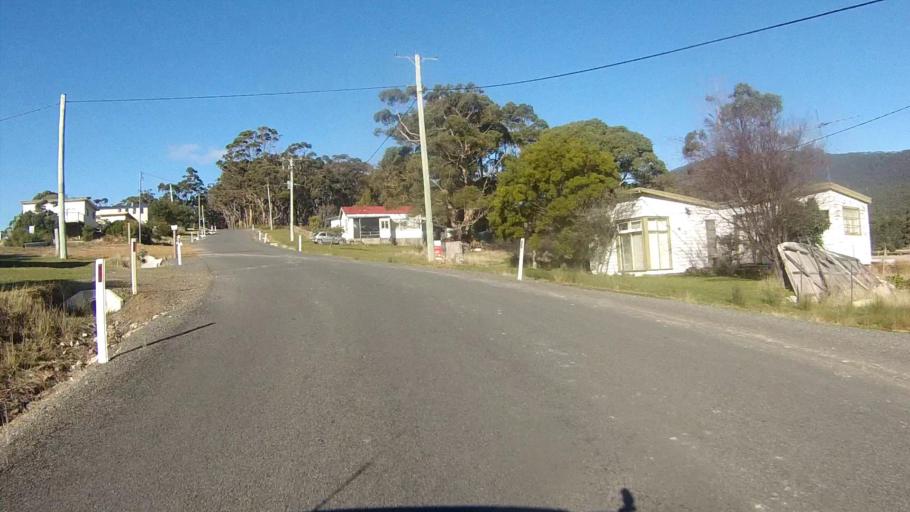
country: AU
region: Tasmania
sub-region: Clarence
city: Sandford
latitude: -43.0380
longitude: 147.9430
